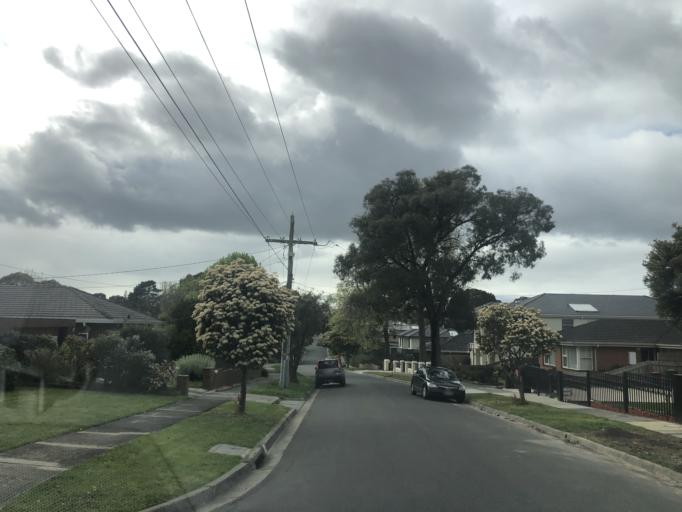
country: AU
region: Victoria
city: Burwood East
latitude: -37.8683
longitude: 145.1448
